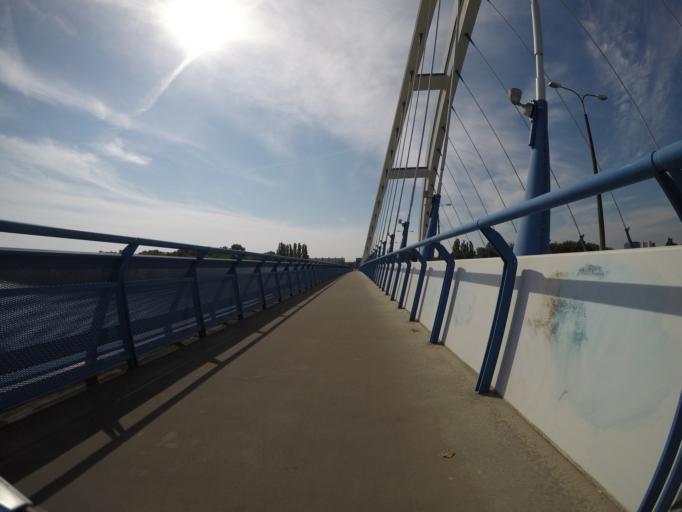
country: SK
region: Bratislavsky
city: Bratislava
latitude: 48.1374
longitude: 17.1283
